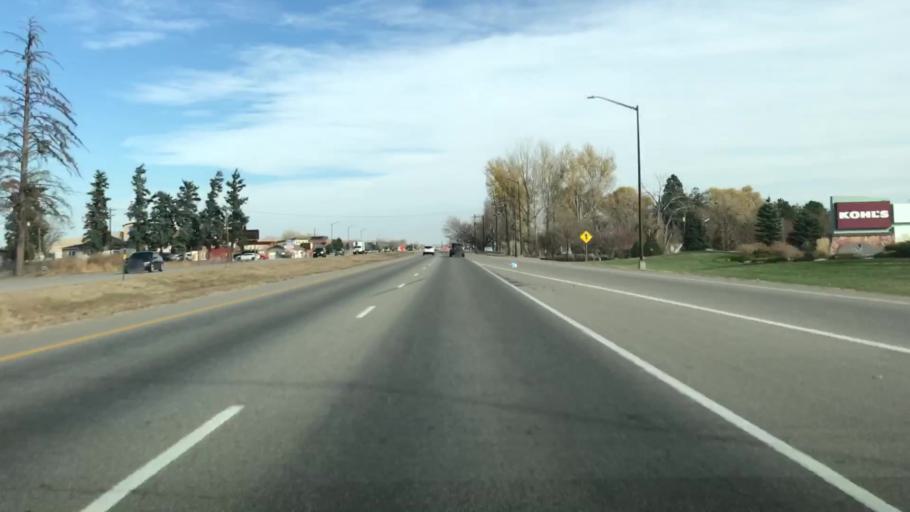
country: US
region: Colorado
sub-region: Larimer County
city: Loveland
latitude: 40.4072
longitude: -105.0336
